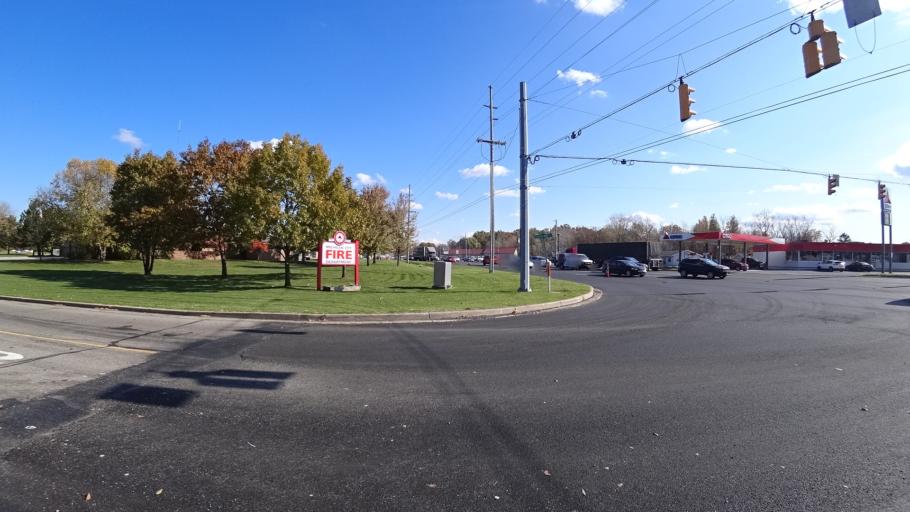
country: US
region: Indiana
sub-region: LaPorte County
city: Michigan City
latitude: 41.6813
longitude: -86.8852
